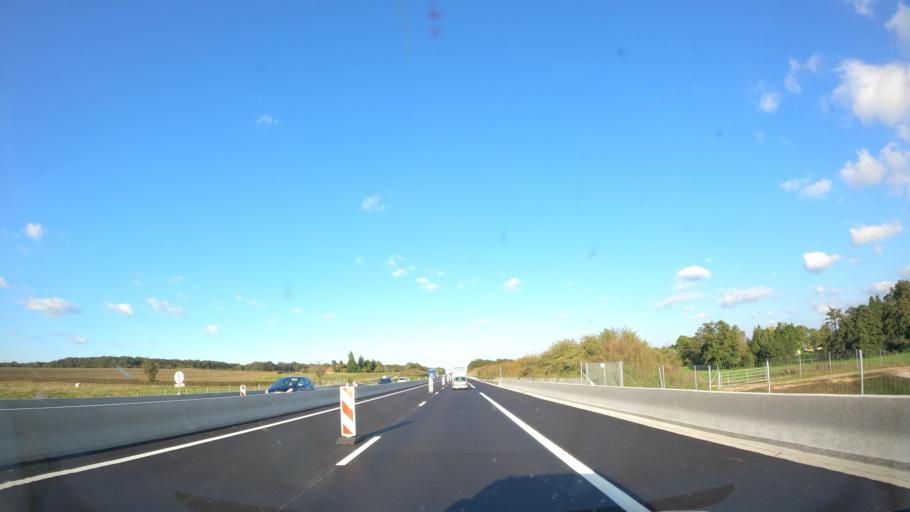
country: FR
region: Bourgogne
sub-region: Departement de Saone-et-Loire
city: Blanzy
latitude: 46.7045
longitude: 4.4169
